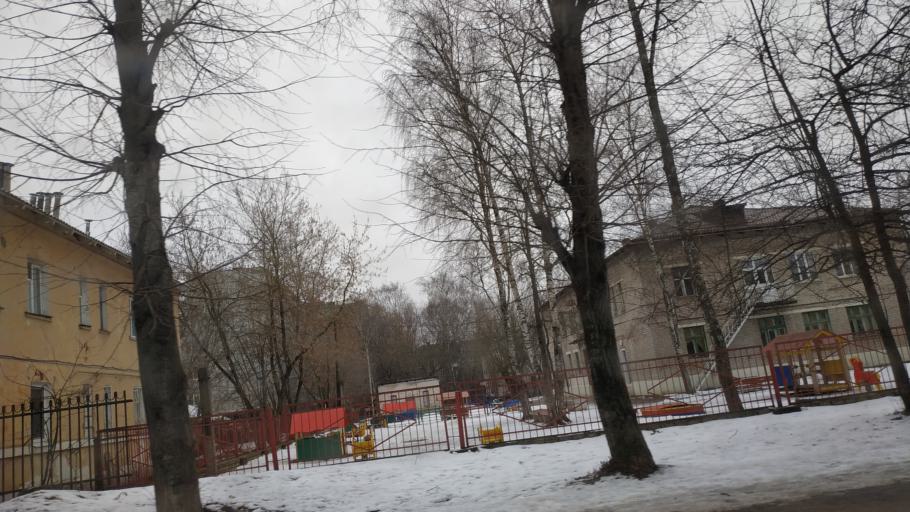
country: RU
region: Tverskaya
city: Tver
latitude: 56.8738
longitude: 35.9031
